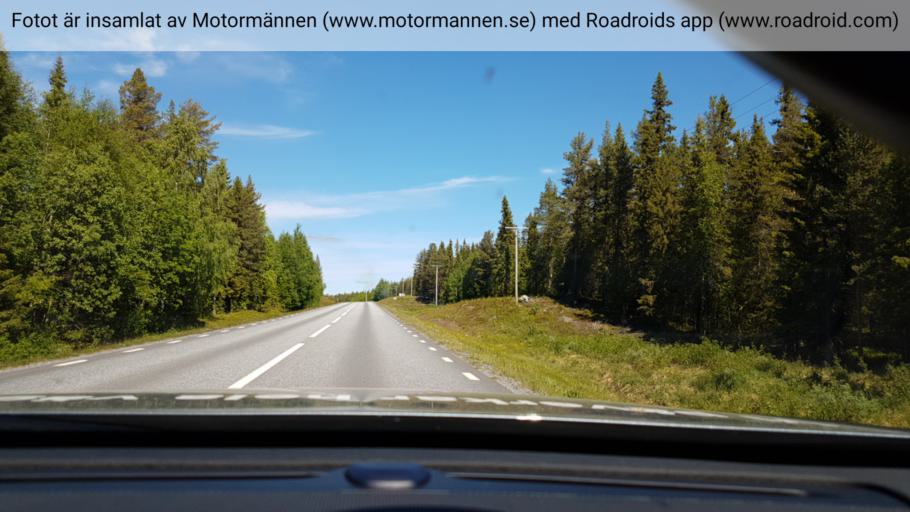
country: SE
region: Vaesterbotten
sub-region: Vilhelmina Kommun
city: Vilhelmina
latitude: 64.5422
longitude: 16.7468
